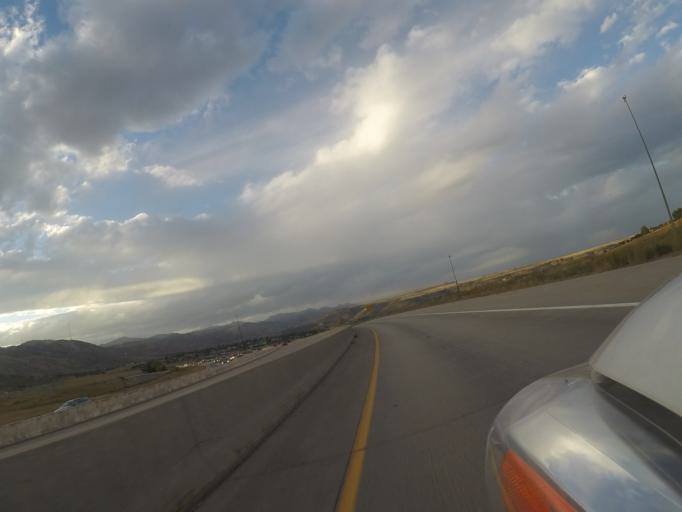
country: US
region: Colorado
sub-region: Jefferson County
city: West Pleasant View
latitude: 39.7100
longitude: -105.1922
